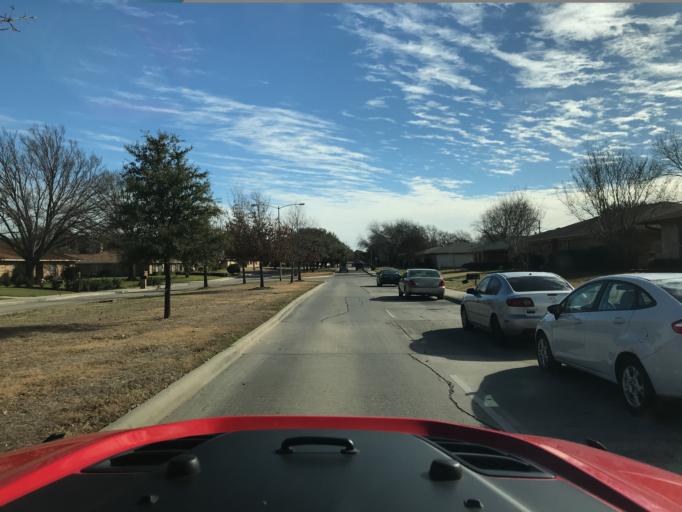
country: US
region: Texas
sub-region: Denton County
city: Lewisville
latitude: 33.0492
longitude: -97.0334
